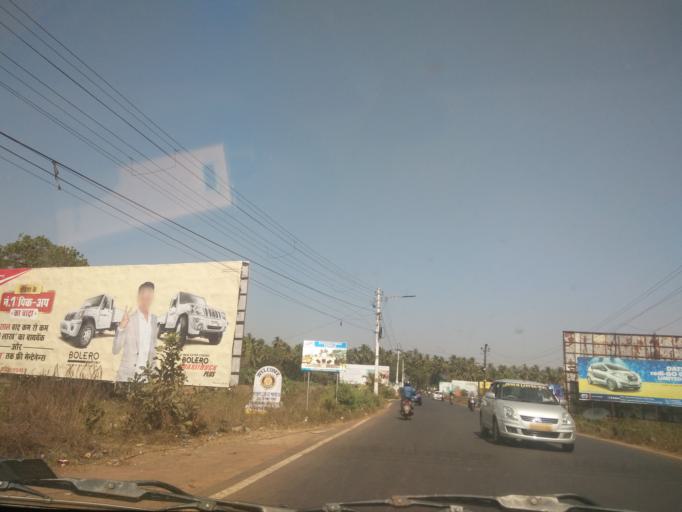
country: IN
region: Goa
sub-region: North Goa
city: Guirim
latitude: 15.5749
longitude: 73.8065
